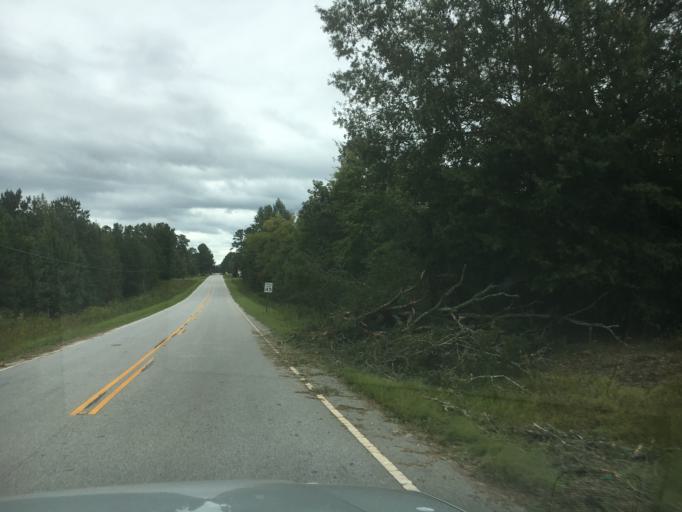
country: US
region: South Carolina
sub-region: Greenwood County
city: Greenwood
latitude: 34.1215
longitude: -82.2472
